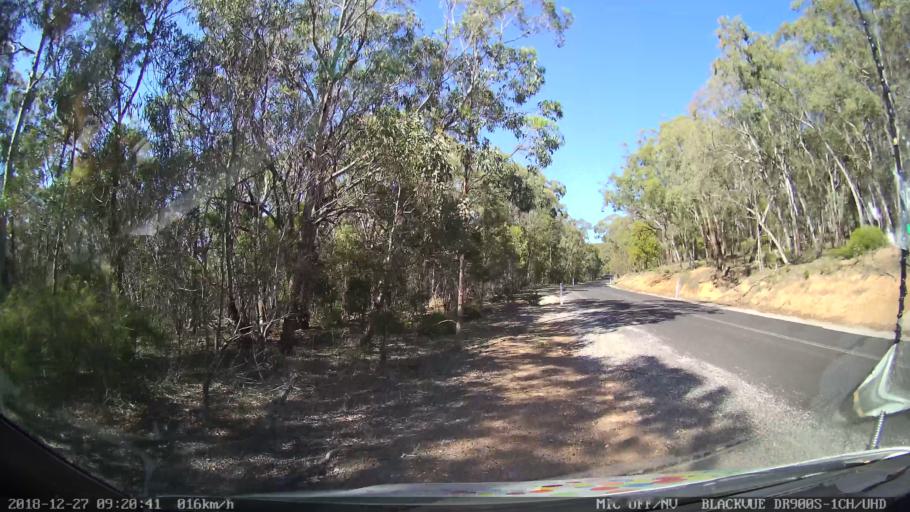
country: AU
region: New South Wales
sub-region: Lithgow
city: Portland
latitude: -33.1211
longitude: 150.0208
